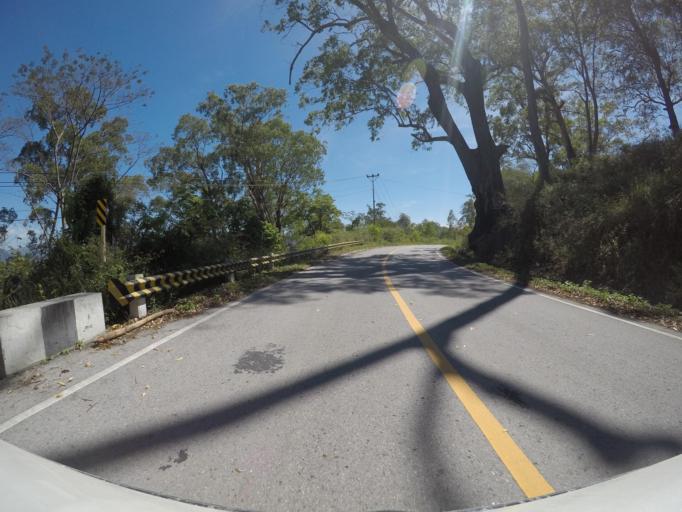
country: TL
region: Manufahi
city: Same
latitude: -8.8899
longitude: 125.9843
